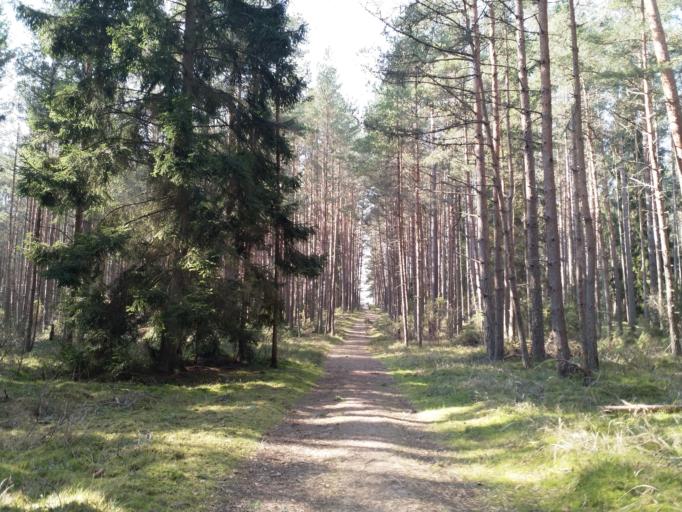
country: LV
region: Alsunga
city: Alsunga
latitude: 57.1596
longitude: 21.4126
